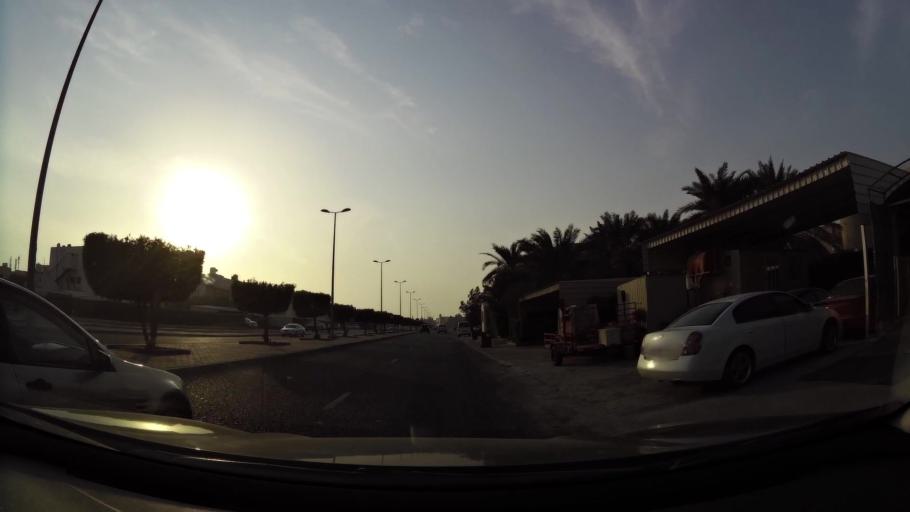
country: KW
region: Mubarak al Kabir
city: Sabah as Salim
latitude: 29.2496
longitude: 48.0748
